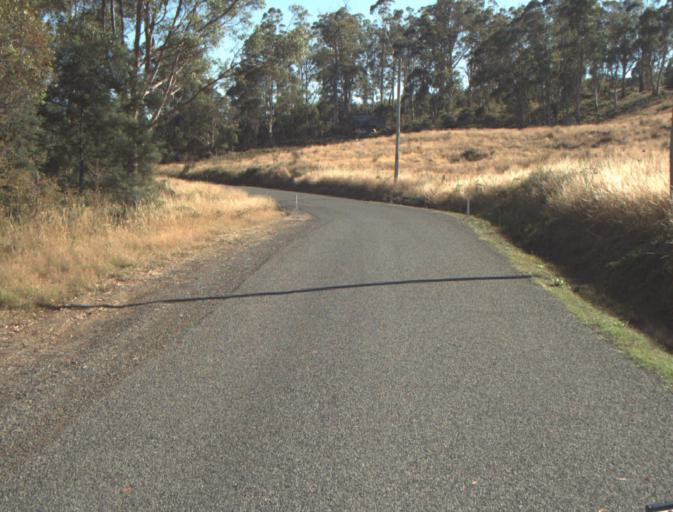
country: AU
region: Tasmania
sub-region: Launceston
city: Newstead
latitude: -41.3586
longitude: 147.3026
